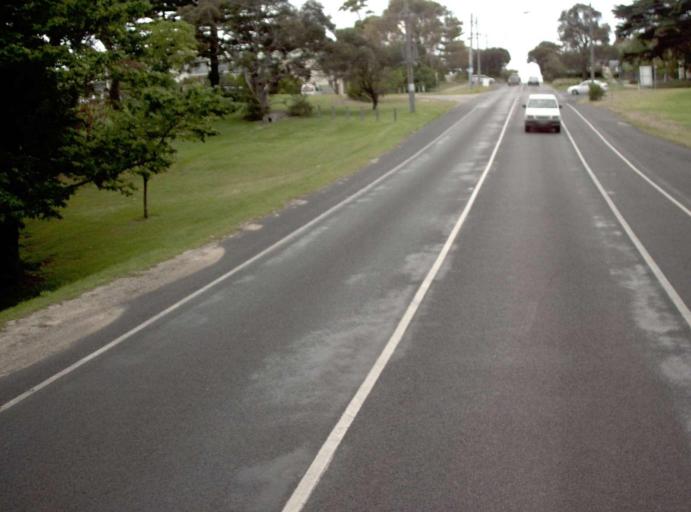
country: AU
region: Victoria
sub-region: Mornington Peninsula
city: Sorrento
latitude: -38.3358
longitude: 144.7404
